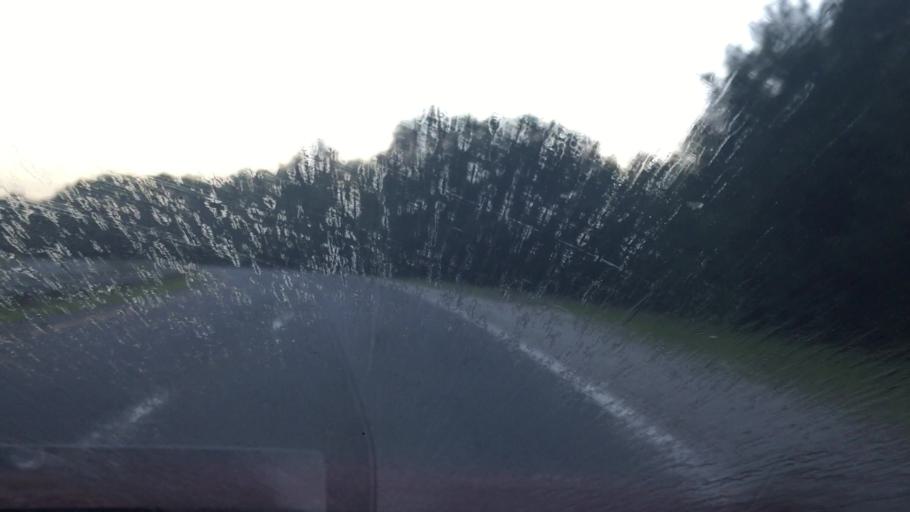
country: US
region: Maine
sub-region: Cumberland County
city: Westbrook
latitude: 43.6735
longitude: -70.3430
